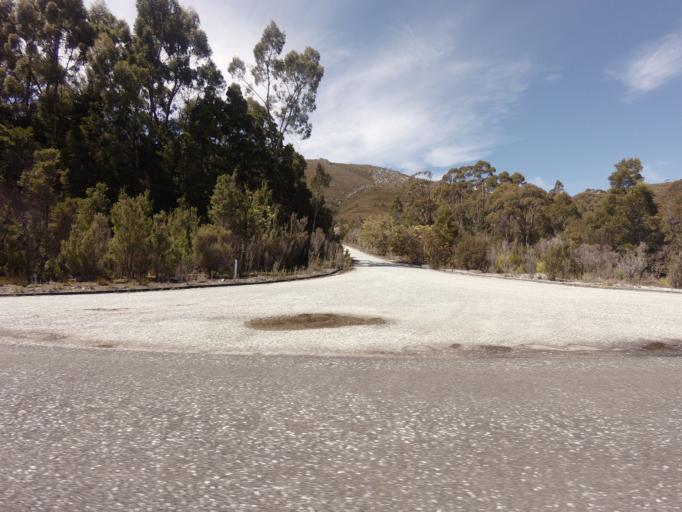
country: AU
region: Tasmania
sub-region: West Coast
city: Queenstown
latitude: -42.7771
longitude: 146.0573
